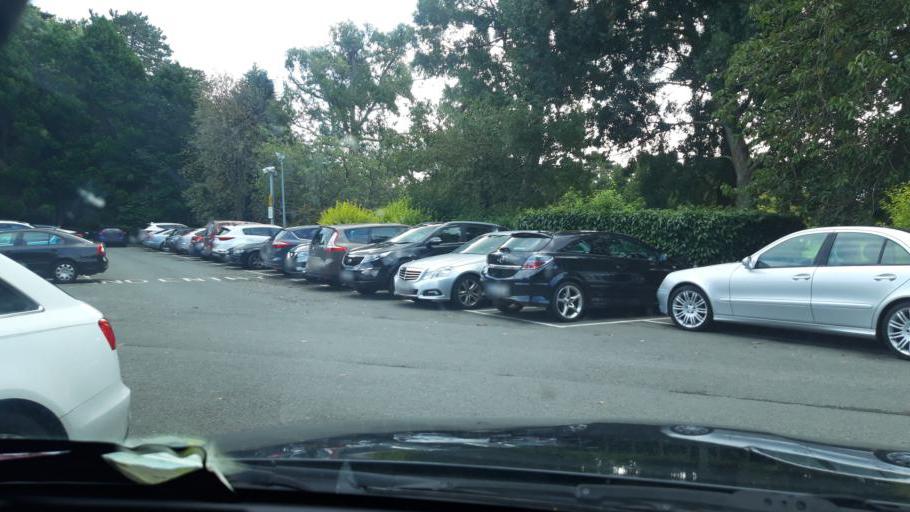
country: IE
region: Leinster
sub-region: Lu
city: Blackrock
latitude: 54.0321
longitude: -6.3535
